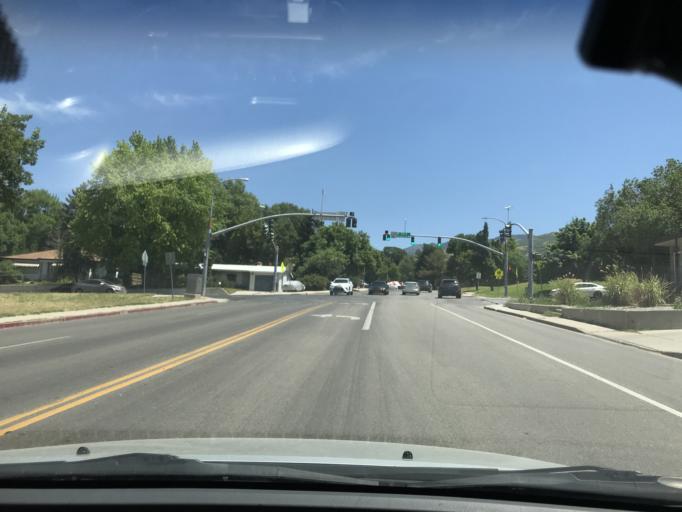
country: US
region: Utah
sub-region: Davis County
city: Woods Cross
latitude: 40.8616
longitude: -111.8864
